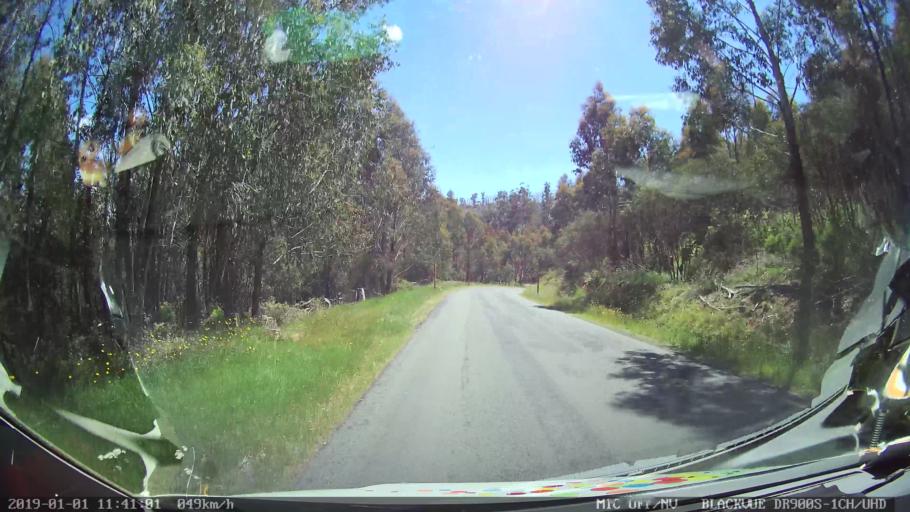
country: AU
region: New South Wales
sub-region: Snowy River
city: Jindabyne
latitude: -35.9168
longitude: 148.3893
